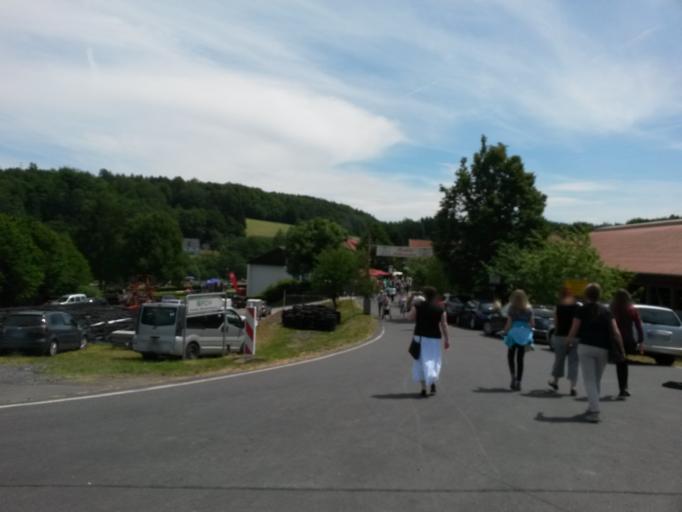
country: DE
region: Hesse
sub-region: Regierungsbezirk Kassel
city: Hilders
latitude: 50.5535
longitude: 9.9325
